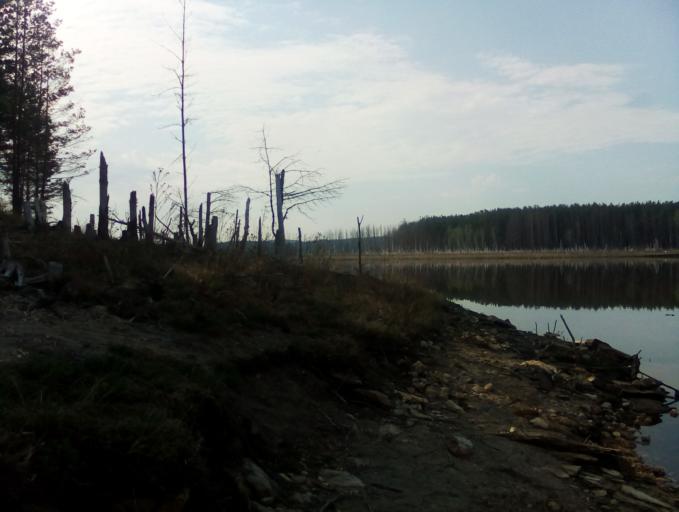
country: RU
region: Chelyabinsk
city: Nizhniy Ufaley
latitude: 55.7541
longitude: 60.1263
